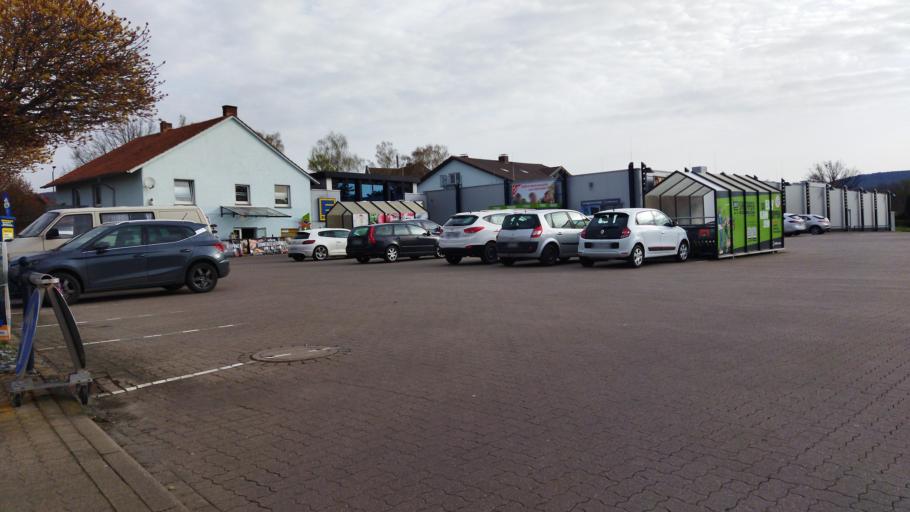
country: DE
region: Lower Saxony
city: Rinteln
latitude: 52.2020
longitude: 9.0140
